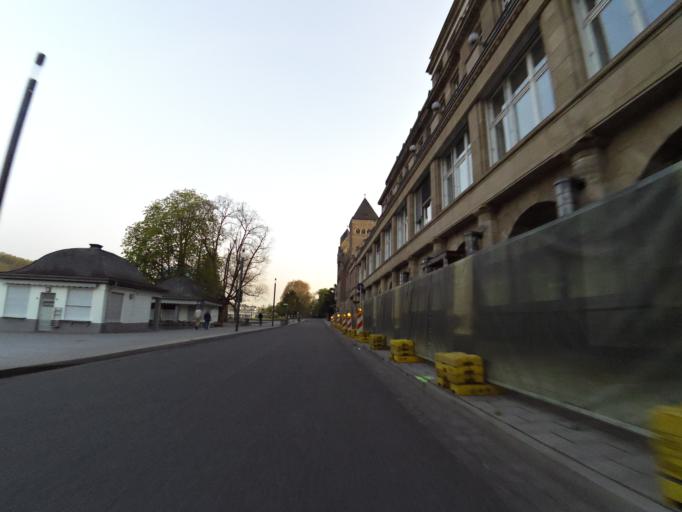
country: DE
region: Rheinland-Pfalz
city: Koblenz
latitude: 50.3594
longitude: 7.6044
